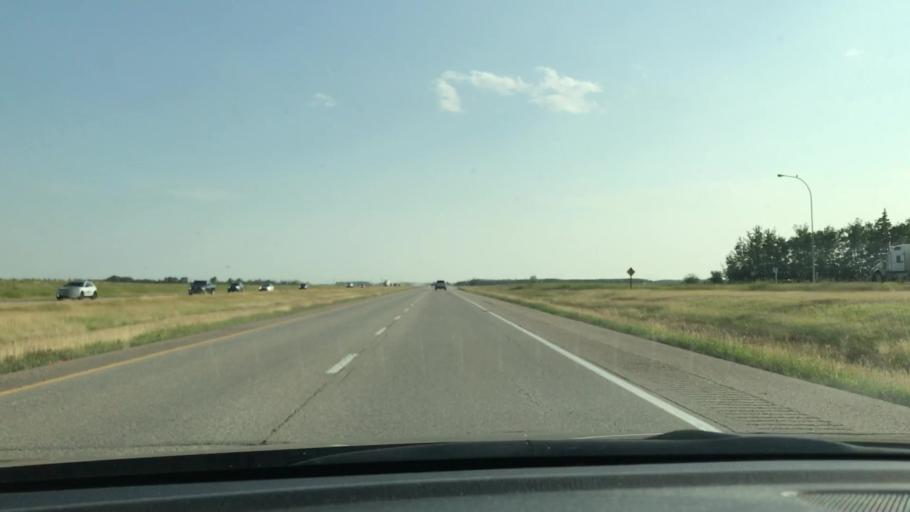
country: CA
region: Alberta
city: Leduc
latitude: 53.2314
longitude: -113.5717
